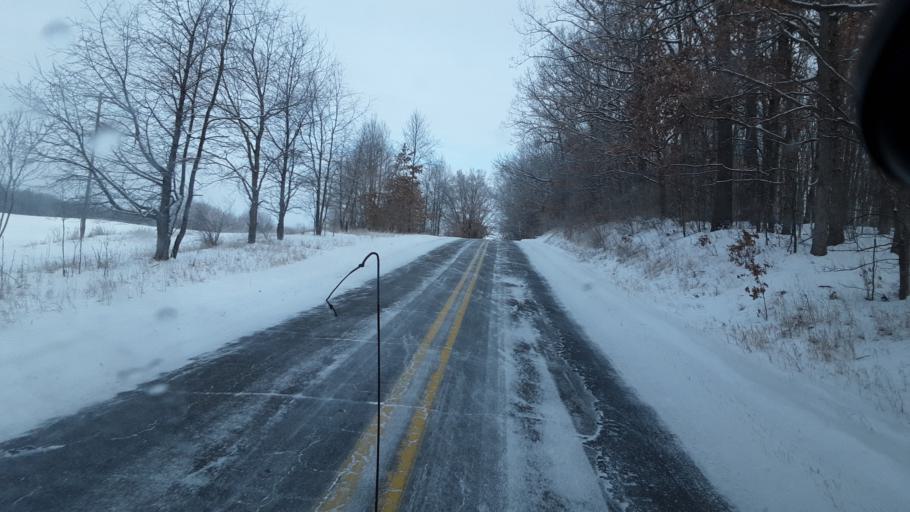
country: US
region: Michigan
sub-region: Ingham County
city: Leslie
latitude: 42.3435
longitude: -84.4827
